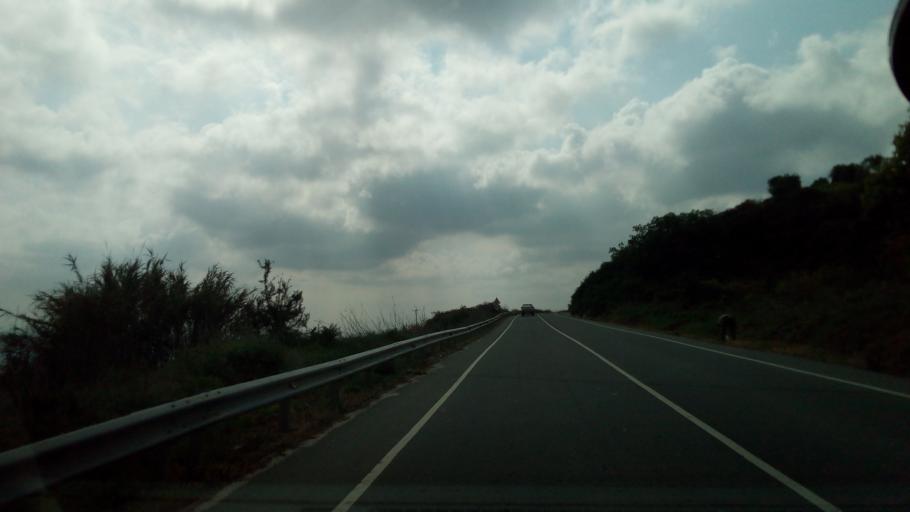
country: CY
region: Pafos
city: Pegeia
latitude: 34.9064
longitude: 32.4407
